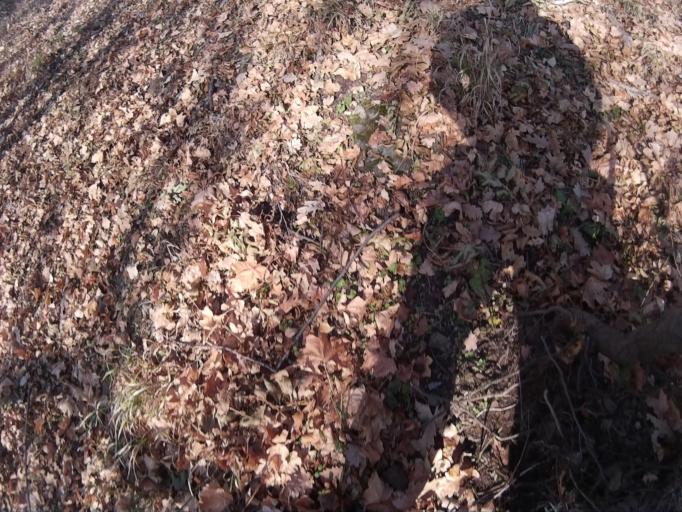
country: HU
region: Heves
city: Belapatfalva
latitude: 48.0304
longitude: 20.3937
